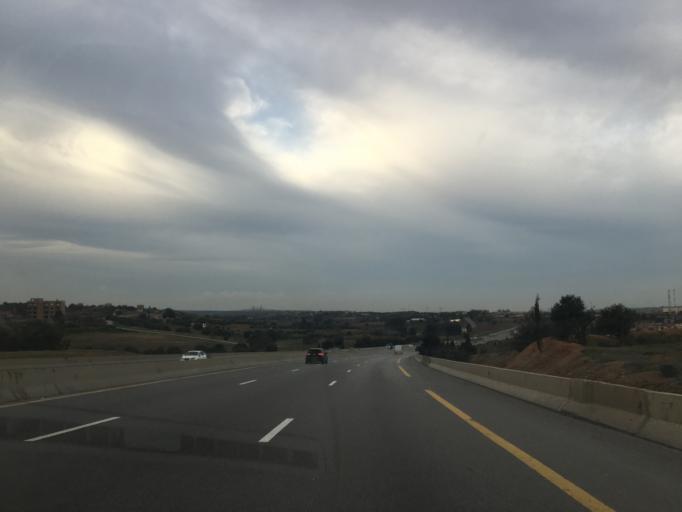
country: DZ
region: Bouira
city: Bouira
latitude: 36.3068
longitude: 4.0773
